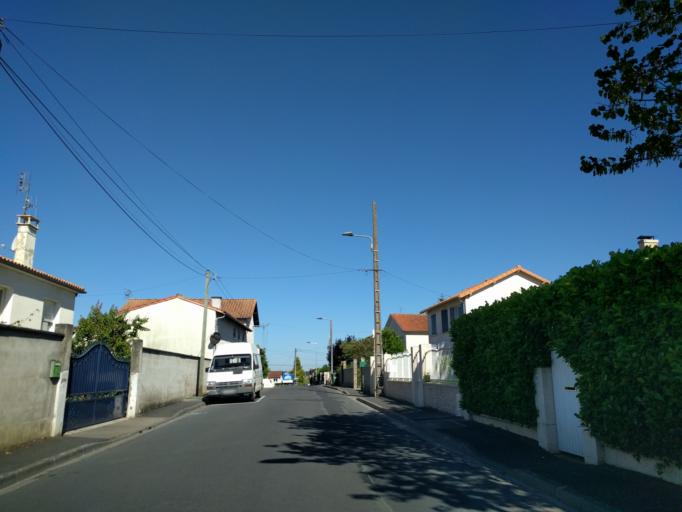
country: FR
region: Poitou-Charentes
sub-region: Departement des Deux-Sevres
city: Niort
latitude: 46.3385
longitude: -0.4452
